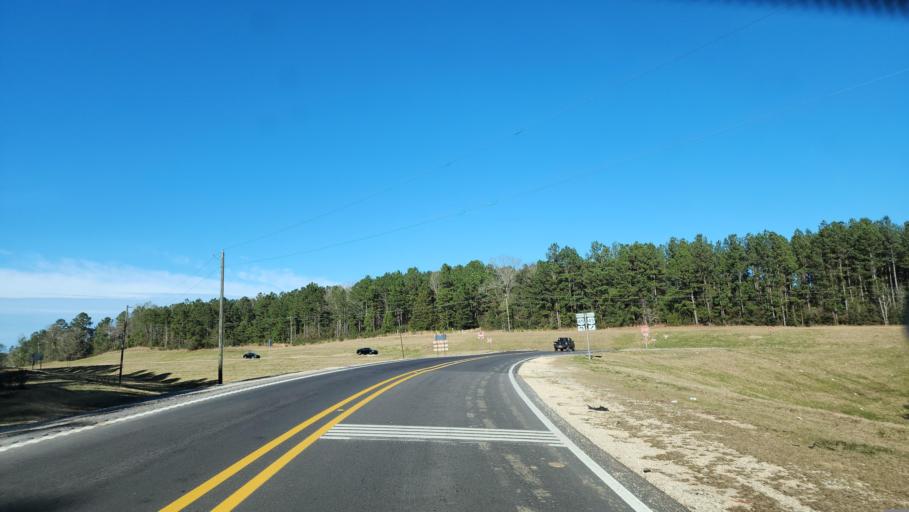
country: US
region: Mississippi
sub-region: Wayne County
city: Waynesboro
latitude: 31.7238
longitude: -88.6441
